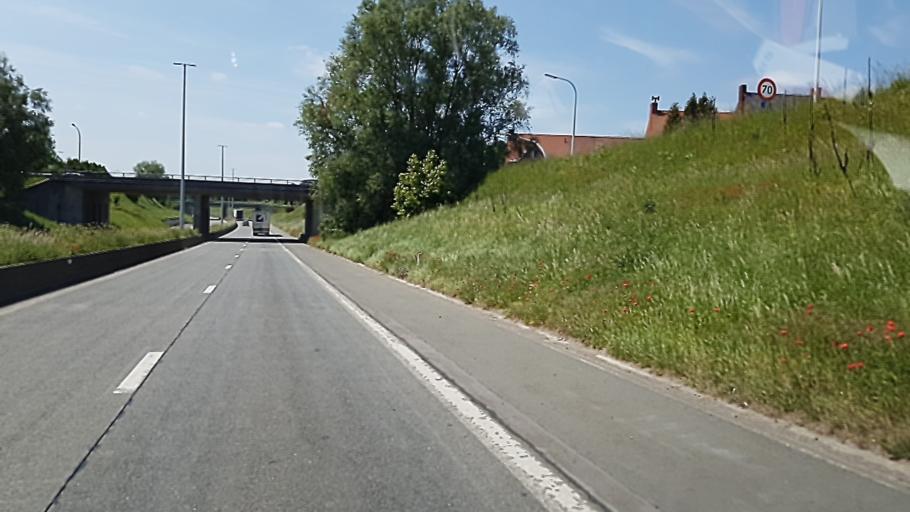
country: BE
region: Flanders
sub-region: Provincie West-Vlaanderen
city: Lendelede
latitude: 50.8490
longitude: 3.2313
